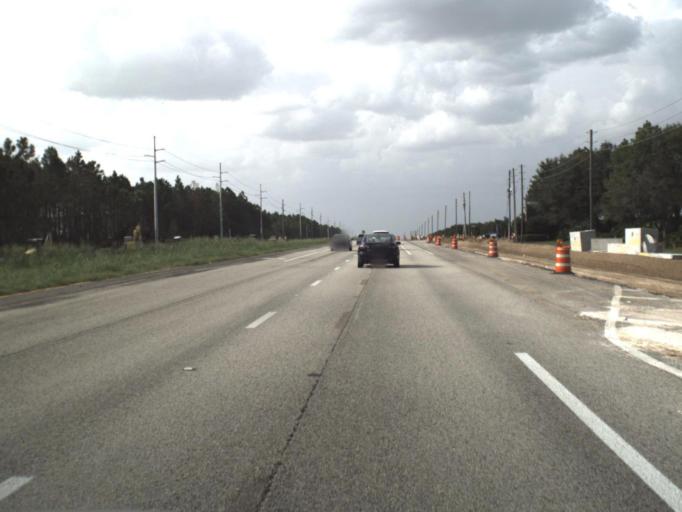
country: US
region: Florida
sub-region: Lake County
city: Four Corners
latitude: 28.3011
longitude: -81.6660
